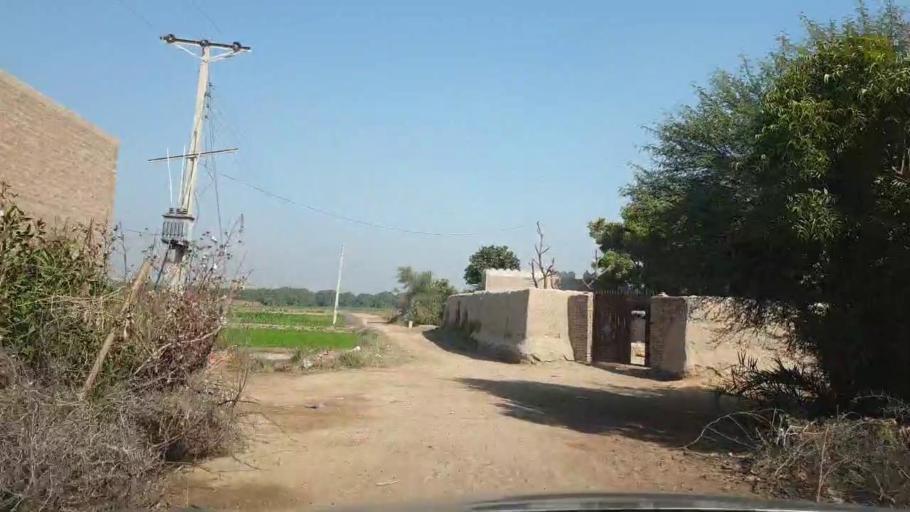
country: PK
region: Sindh
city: Tando Allahyar
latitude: 25.5305
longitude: 68.7186
